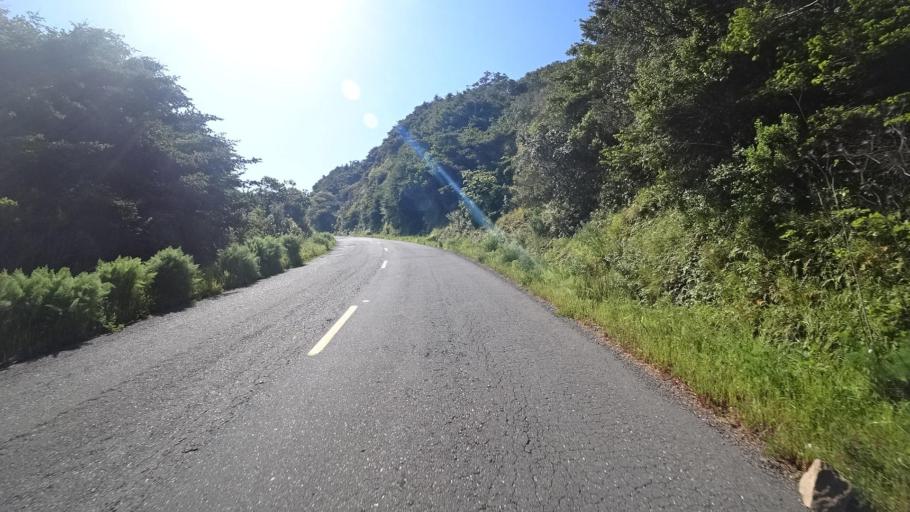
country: US
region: California
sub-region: Humboldt County
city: Ferndale
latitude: 40.3498
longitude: -124.3576
